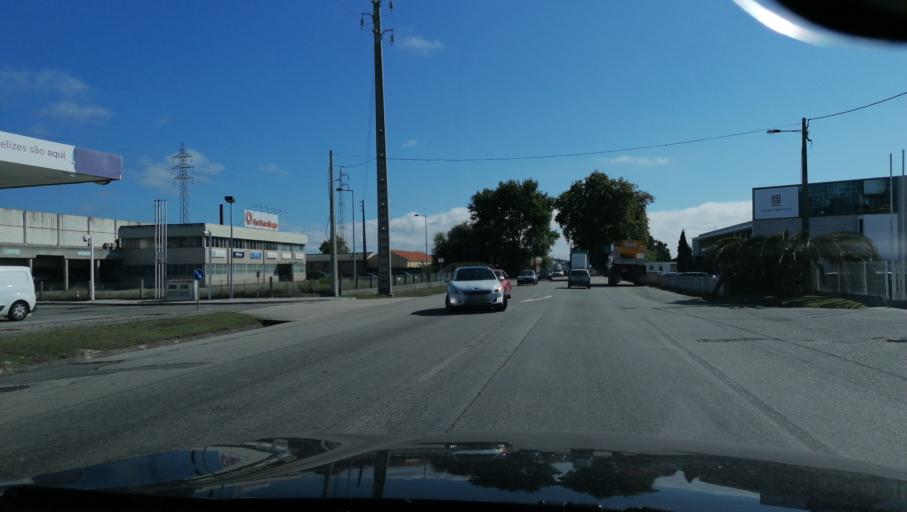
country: PT
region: Aveiro
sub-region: Aveiro
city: Aveiro
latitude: 40.6617
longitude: -8.6129
